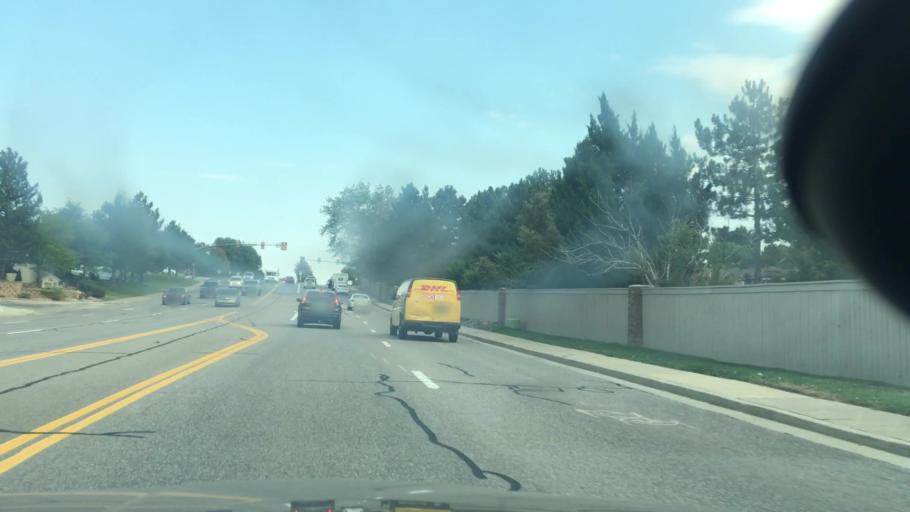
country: US
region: Colorado
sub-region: Arapahoe County
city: Centennial
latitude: 39.5806
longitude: -104.8878
